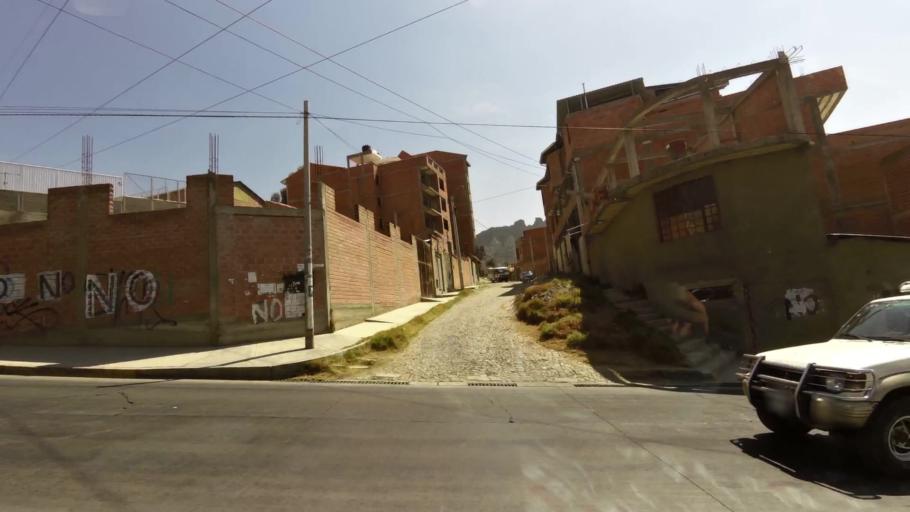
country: BO
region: La Paz
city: La Paz
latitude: -16.5321
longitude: -68.1303
